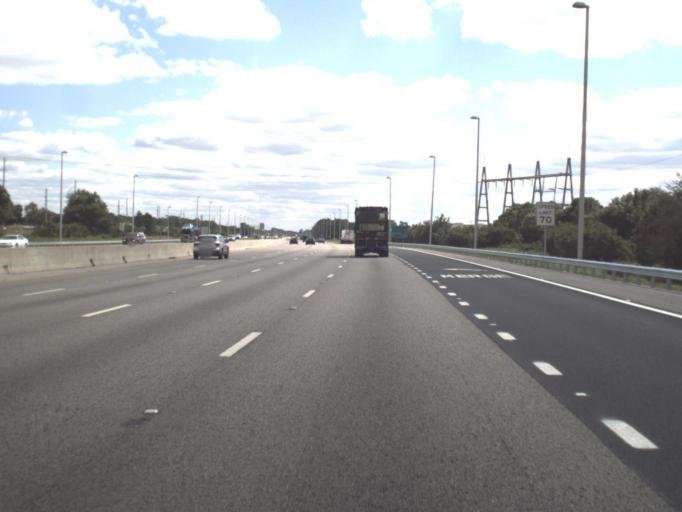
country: US
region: Florida
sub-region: Orange County
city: Tangelo Park
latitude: 28.4706
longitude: -81.4433
